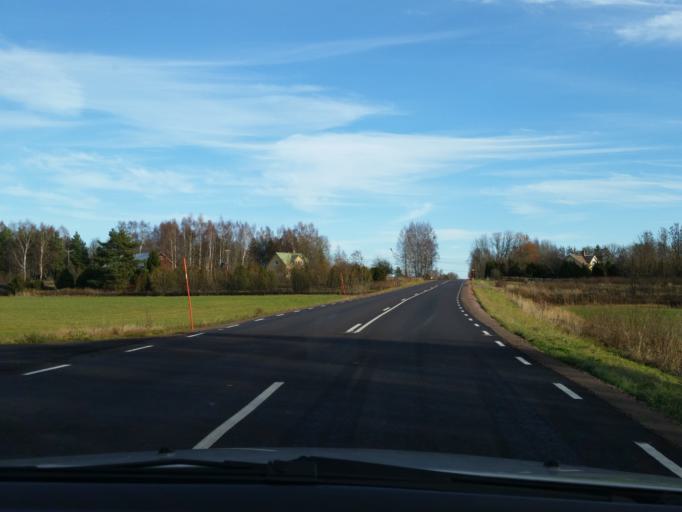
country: AX
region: Alands landsbygd
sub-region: Finstroem
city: Finstroem
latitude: 60.3160
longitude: 19.9829
